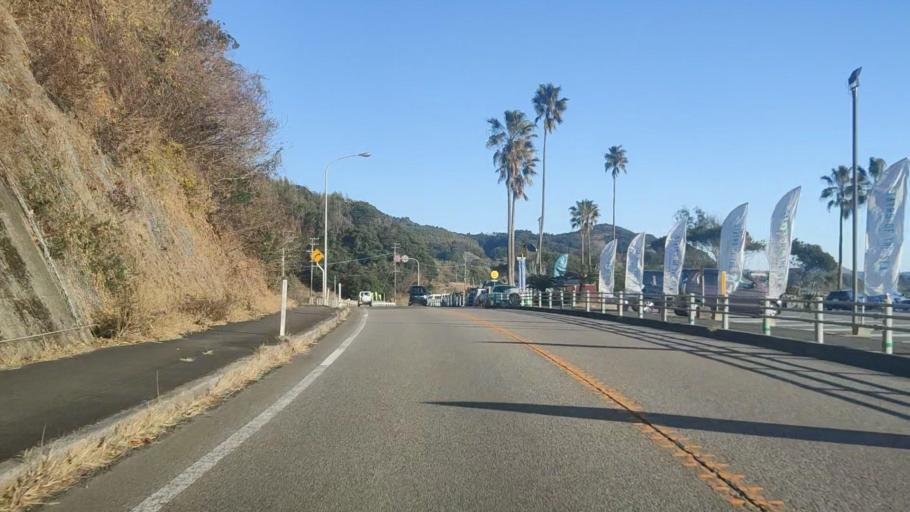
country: JP
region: Miyazaki
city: Nobeoka
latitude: 32.3587
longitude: 131.6219
